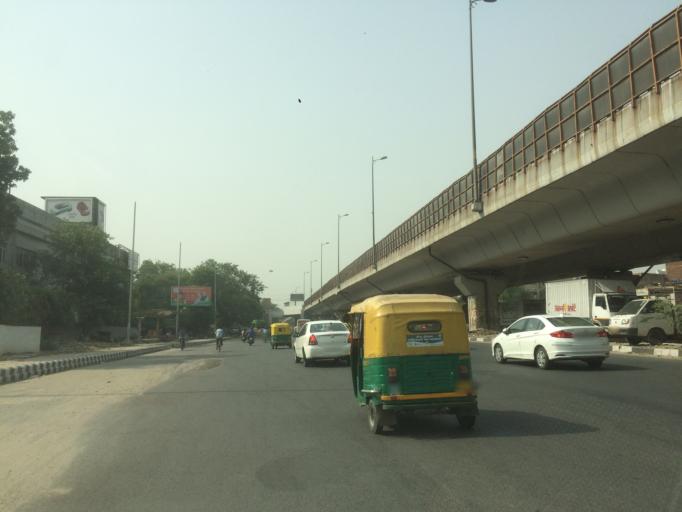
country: IN
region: NCT
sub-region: Central Delhi
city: Karol Bagh
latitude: 28.6279
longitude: 77.1339
